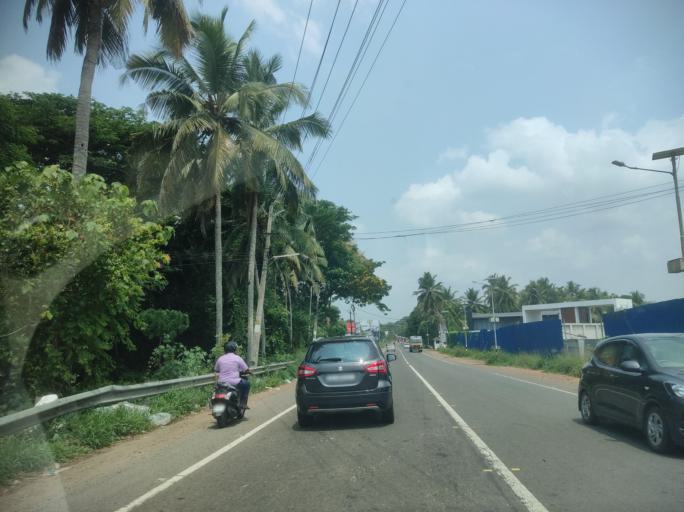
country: IN
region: Kerala
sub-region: Kottayam
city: Changanacheri
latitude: 9.4143
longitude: 76.5525
